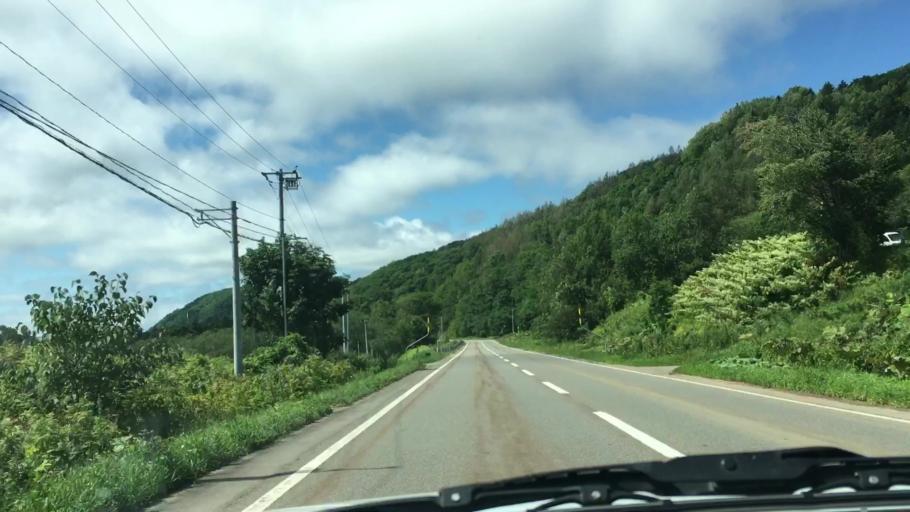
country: JP
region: Hokkaido
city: Kitami
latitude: 43.3612
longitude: 143.8305
